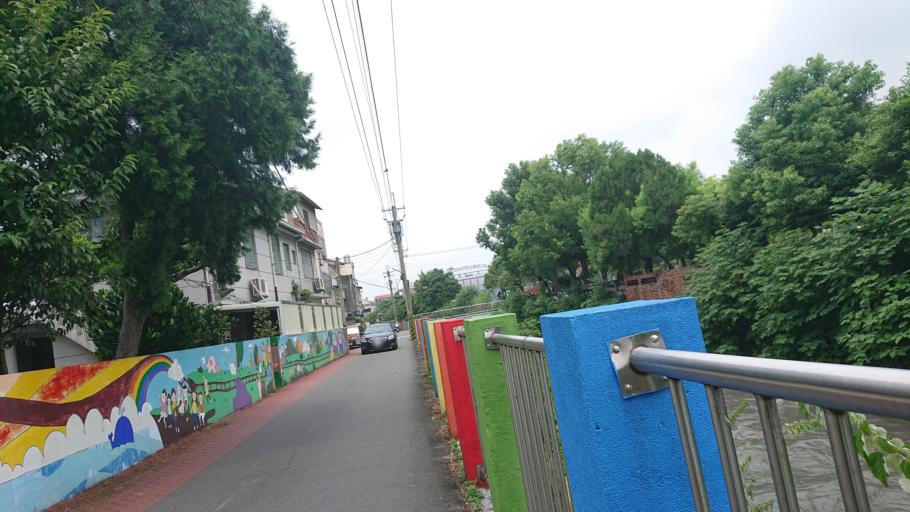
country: TW
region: Taiwan
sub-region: Nantou
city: Nantou
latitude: 23.8096
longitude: 120.6182
